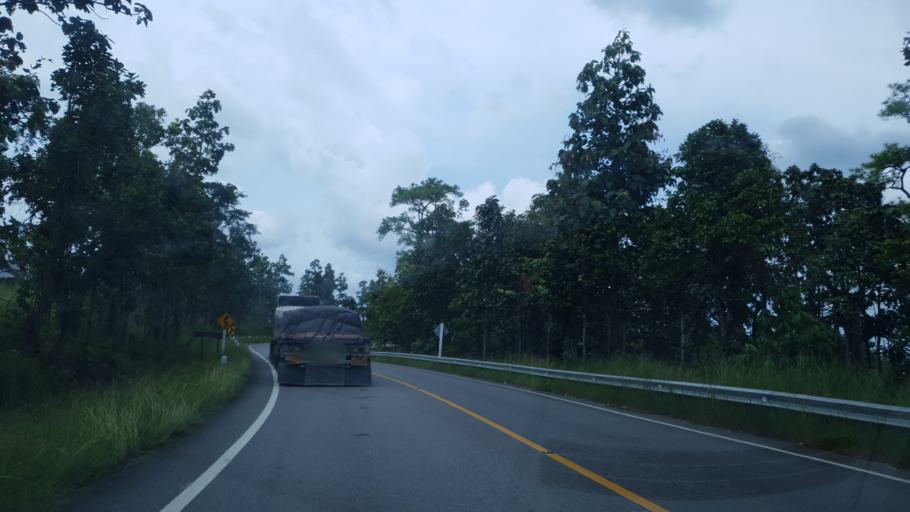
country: TH
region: Mae Hong Son
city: Khun Yuam
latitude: 18.7974
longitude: 97.9319
